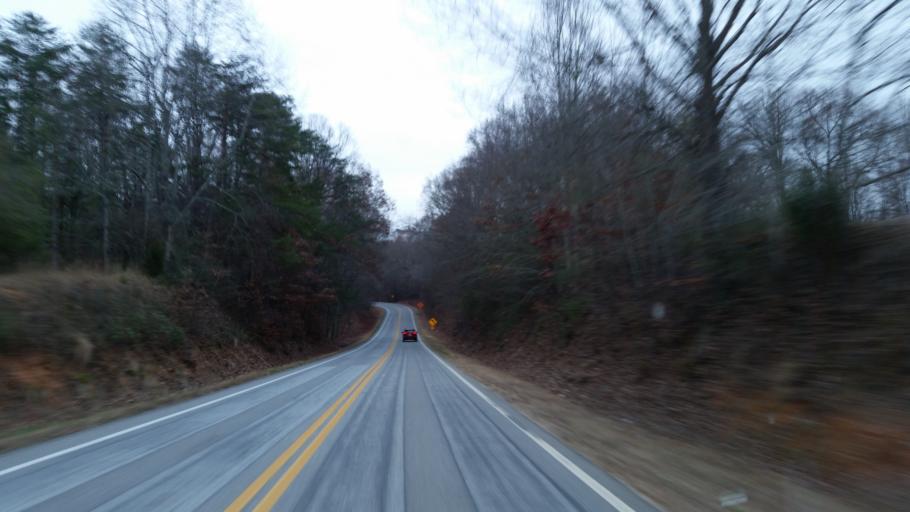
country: US
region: Georgia
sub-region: Dawson County
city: Dawsonville
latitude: 34.4158
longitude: -84.0298
